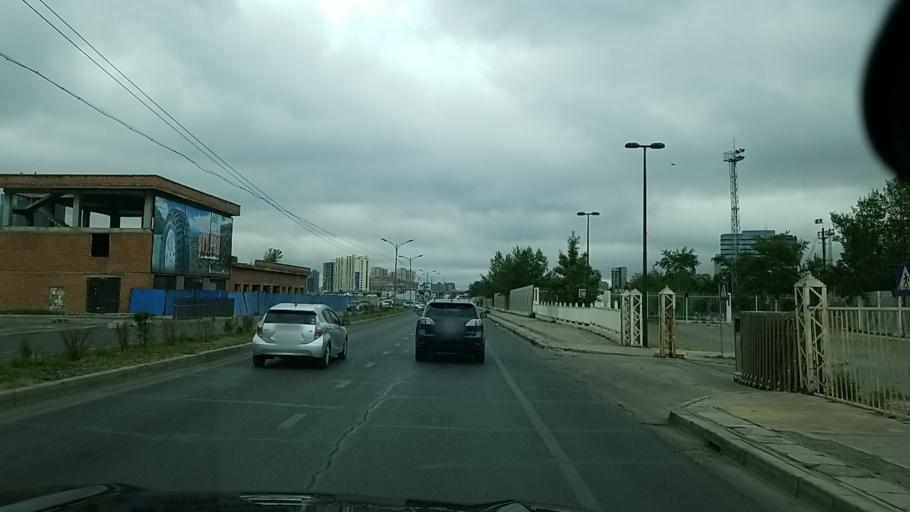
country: MN
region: Ulaanbaatar
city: Ulaanbaatar
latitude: 47.9083
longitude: 106.9221
